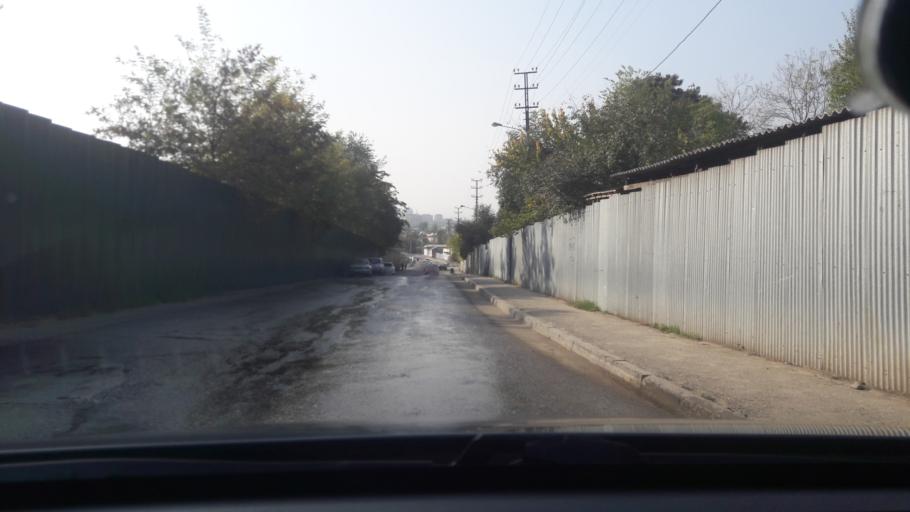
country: TJ
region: Dushanbe
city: Dushanbe
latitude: 38.5628
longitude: 68.7832
